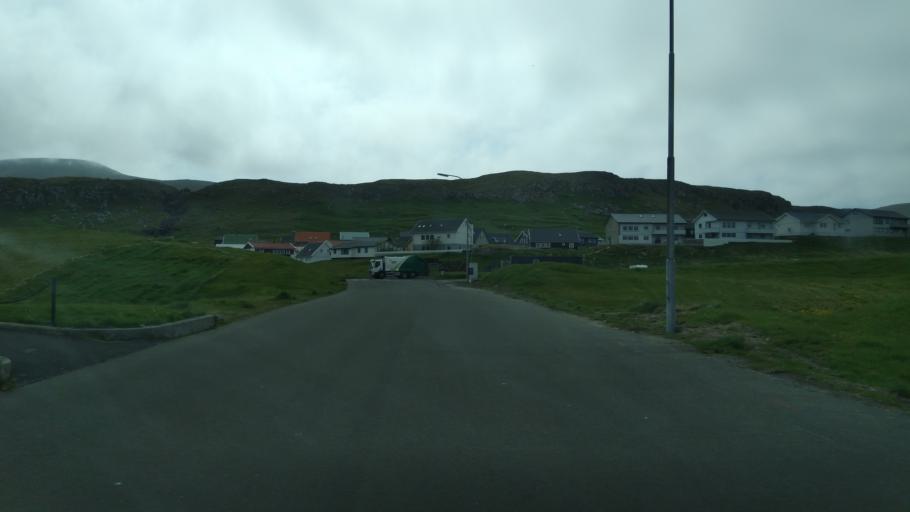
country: FO
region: Sandoy
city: Sandur
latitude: 61.9047
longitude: -6.8869
